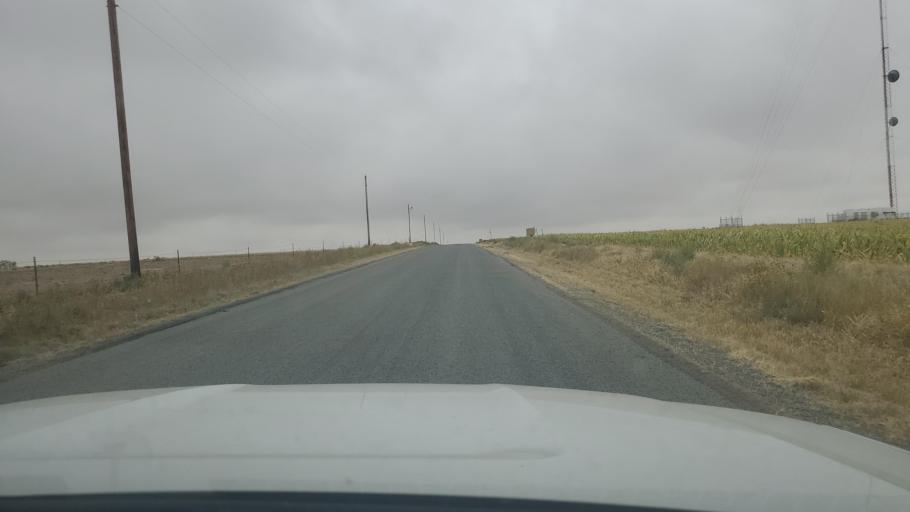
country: US
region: Colorado
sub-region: Weld County
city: Lochbuie
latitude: 39.9186
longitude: -104.6028
